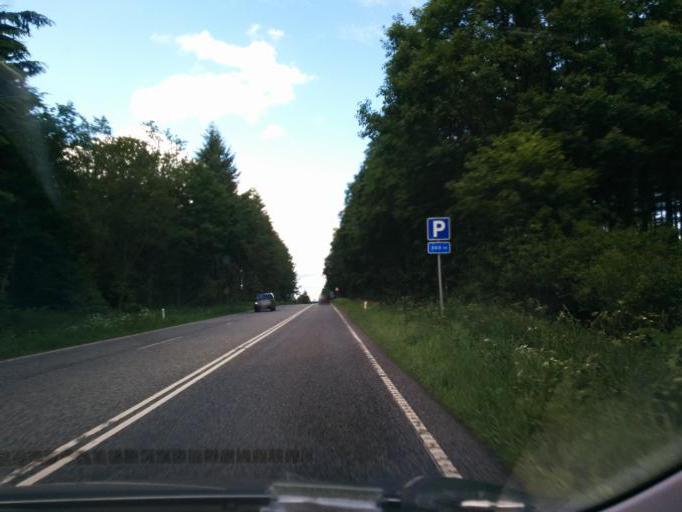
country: DK
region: Central Jutland
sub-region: Syddjurs Kommune
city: Ebeltoft
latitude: 56.2539
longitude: 10.6372
